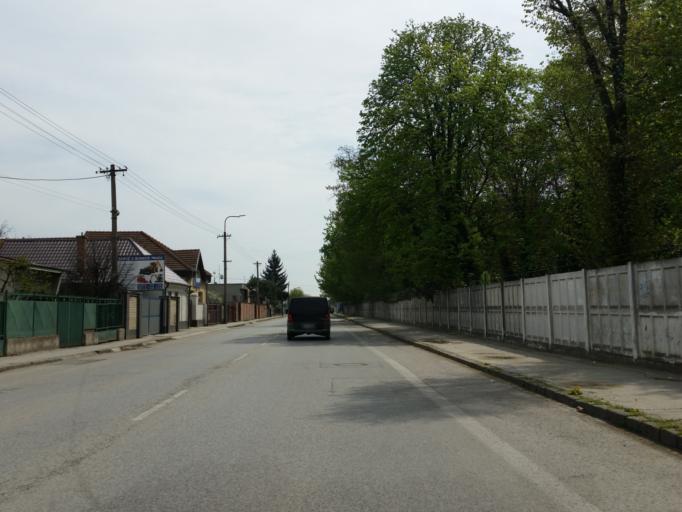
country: SK
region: Trnavsky
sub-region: Okres Galanta
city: Galanta
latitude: 48.2778
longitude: 17.7409
